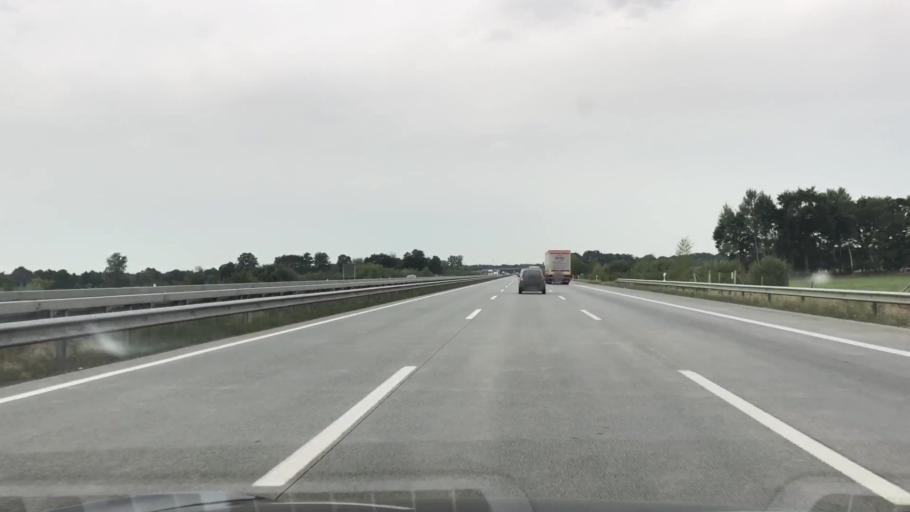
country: DE
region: Lower Saxony
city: Gross Meckelsen
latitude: 53.2473
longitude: 9.4150
